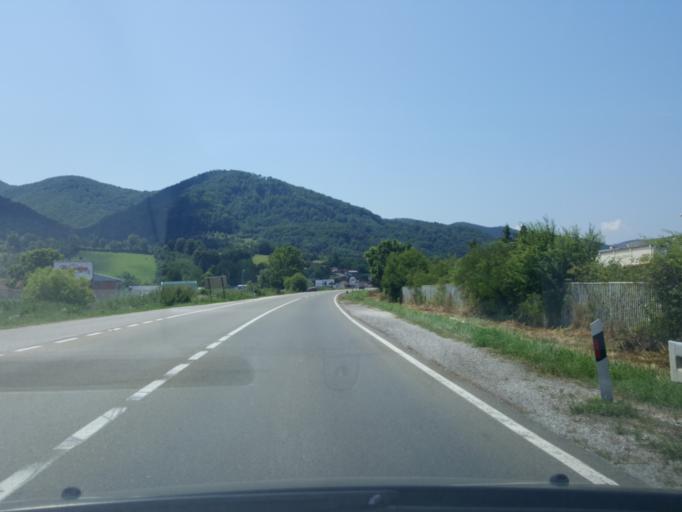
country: RS
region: Central Serbia
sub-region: Moravicki Okrug
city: Gornji Milanovac
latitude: 44.0076
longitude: 20.4610
